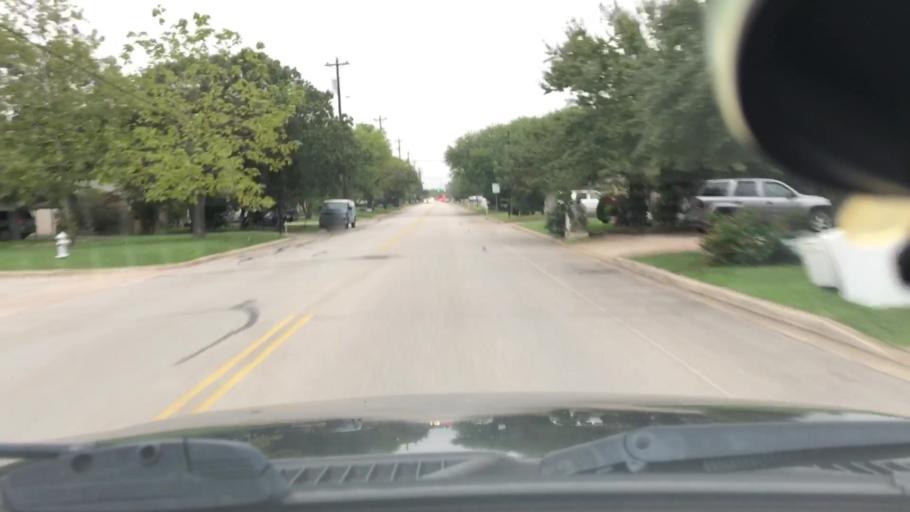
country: US
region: Texas
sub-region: Williamson County
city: Leander
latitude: 30.5432
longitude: -97.8450
